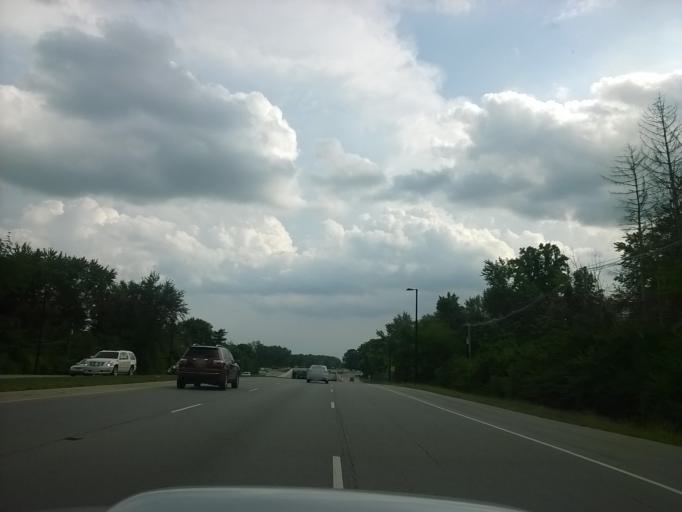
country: US
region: Indiana
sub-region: Hamilton County
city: Carmel
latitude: 39.9748
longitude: -86.1129
